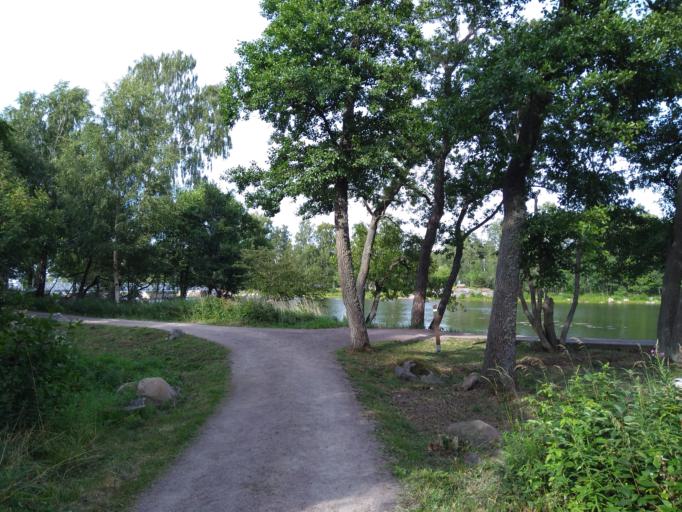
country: FI
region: Uusimaa
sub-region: Helsinki
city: Helsinki
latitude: 60.1386
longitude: 24.9183
